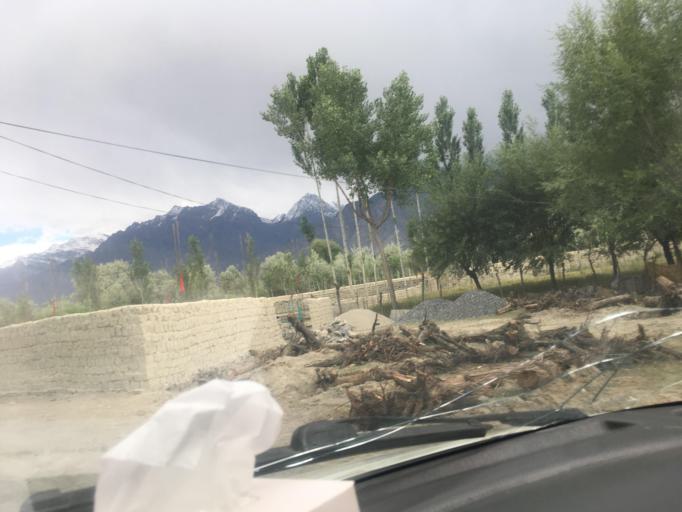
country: PK
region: Gilgit-Baltistan
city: Skardu
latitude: 35.3180
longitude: 75.5528
